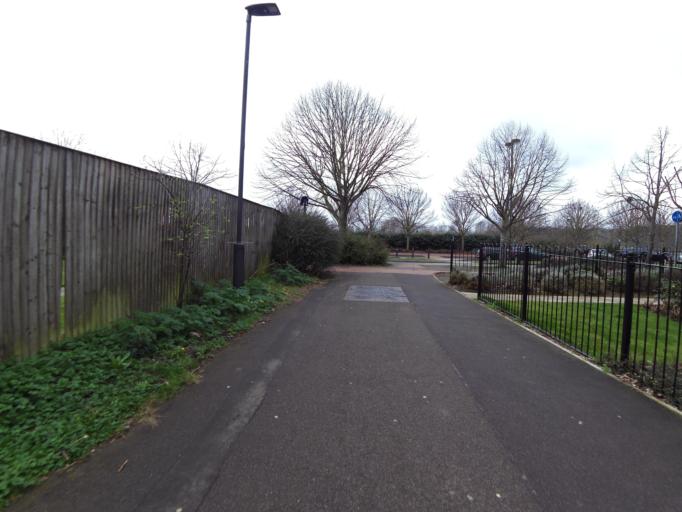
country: GB
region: England
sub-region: Doncaster
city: Doncaster
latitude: 53.5101
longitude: -1.1018
